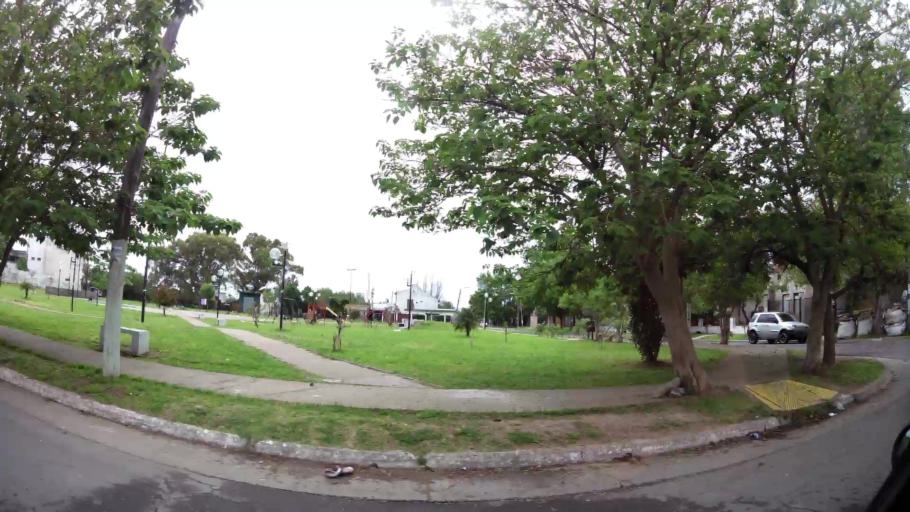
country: AR
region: Buenos Aires
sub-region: Partido de Quilmes
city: Quilmes
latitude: -34.7541
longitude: -58.2054
